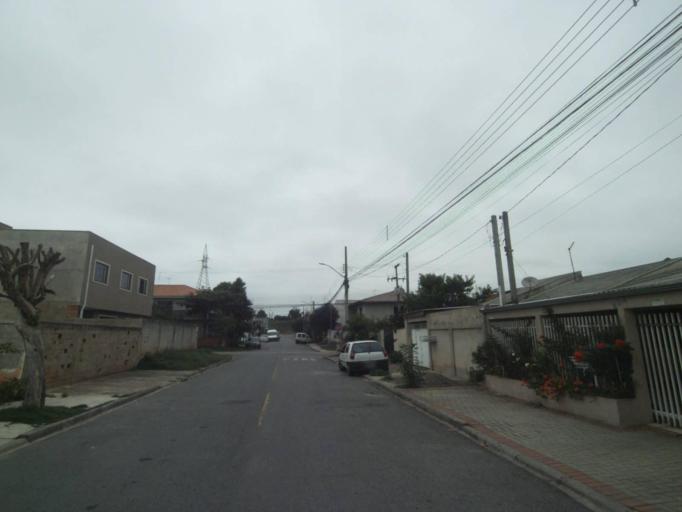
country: BR
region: Parana
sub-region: Araucaria
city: Araucaria
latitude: -25.5513
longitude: -49.3379
